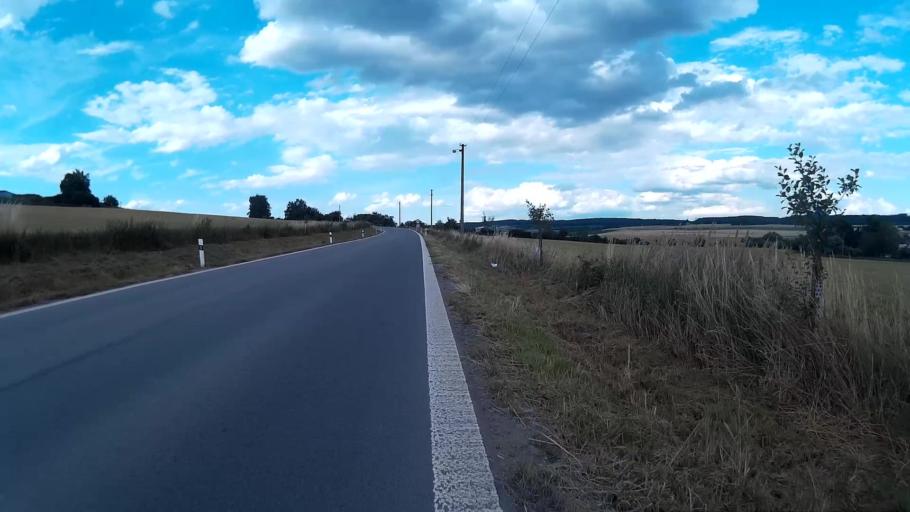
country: CZ
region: South Moravian
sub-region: Okres Brno-Venkov
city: Rosice
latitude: 49.1876
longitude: 16.3892
